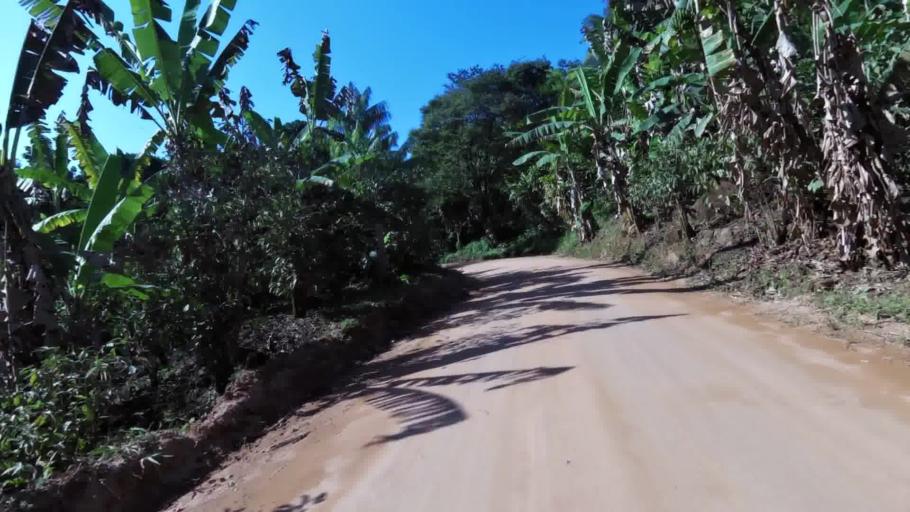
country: BR
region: Espirito Santo
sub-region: Alfredo Chaves
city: Alfredo Chaves
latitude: -20.5591
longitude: -40.7301
